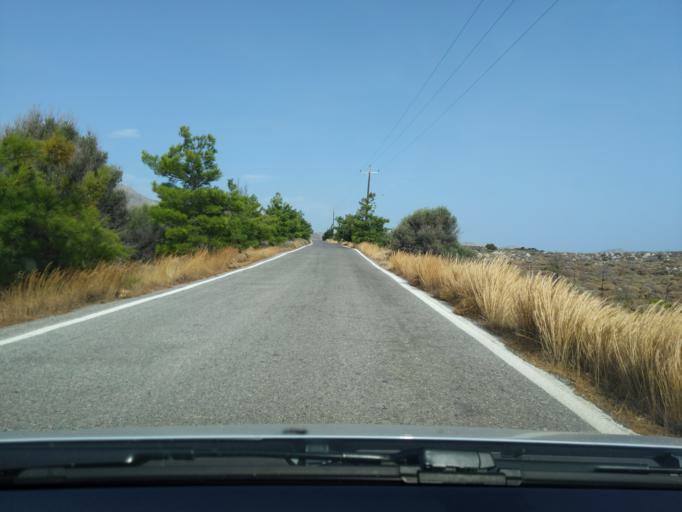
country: GR
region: Crete
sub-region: Nomos Lasithiou
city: Palekastro
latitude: 35.0887
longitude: 26.2414
